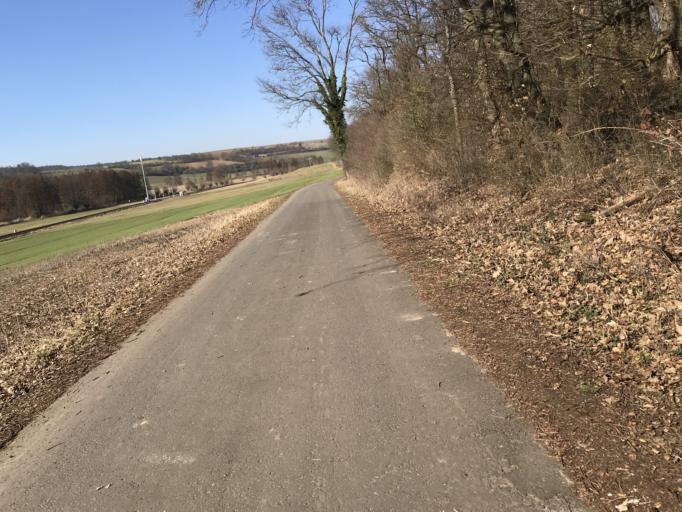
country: DE
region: Hesse
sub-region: Regierungsbezirk Darmstadt
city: Ranstadt
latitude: 50.3851
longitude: 8.9822
